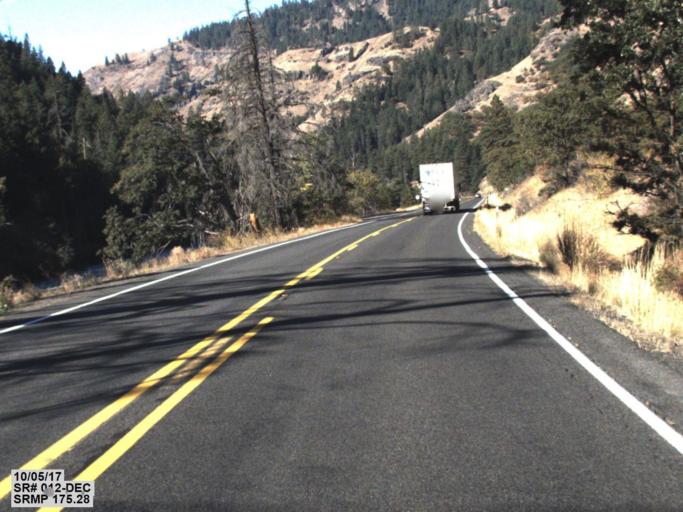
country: US
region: Washington
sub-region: Yakima County
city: Tieton
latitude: 46.6833
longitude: -120.9449
